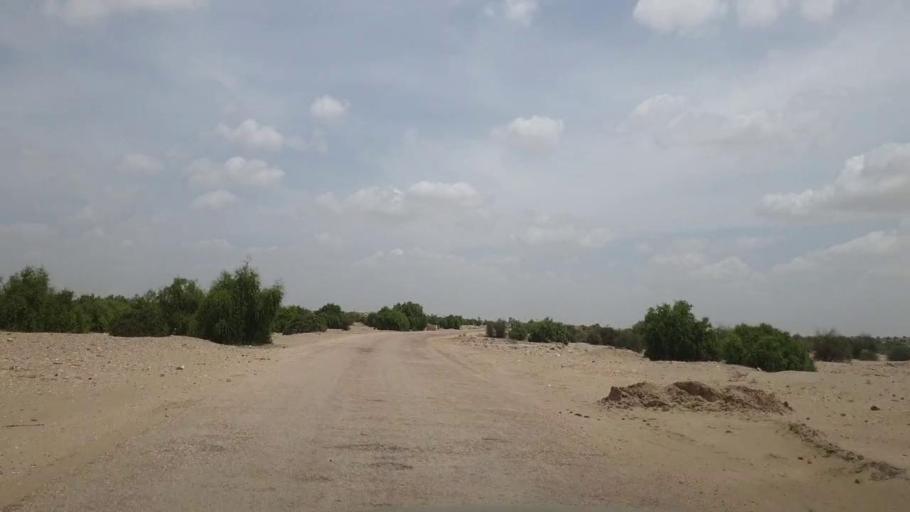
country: PK
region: Sindh
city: Kot Diji
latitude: 27.1935
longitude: 69.1645
